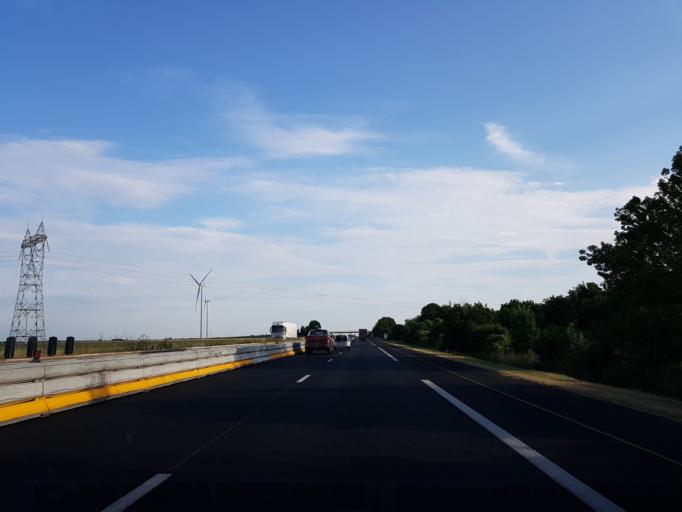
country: FR
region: Picardie
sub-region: Departement de la Somme
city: Roye
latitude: 49.6719
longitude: 2.7707
